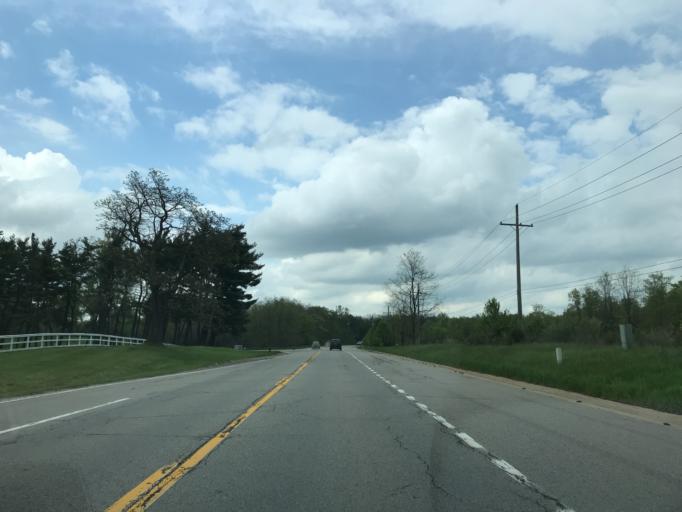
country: US
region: Michigan
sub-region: Oakland County
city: South Lyon
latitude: 42.5092
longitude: -83.6595
